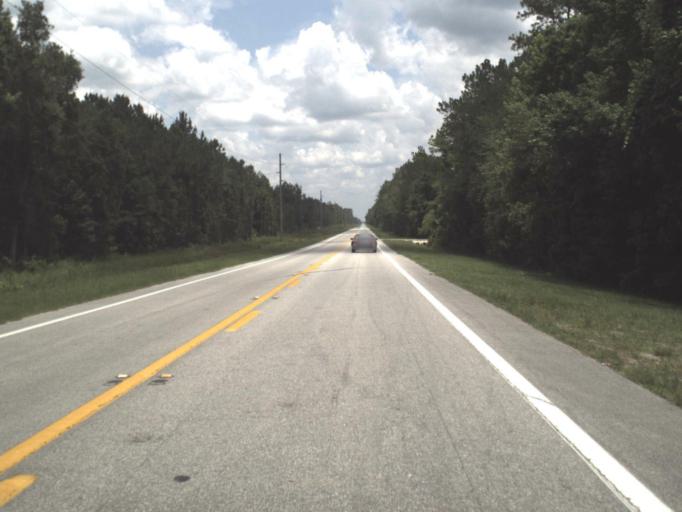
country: US
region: Florida
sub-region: Levy County
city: Bronson
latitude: 29.3550
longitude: -82.7343
